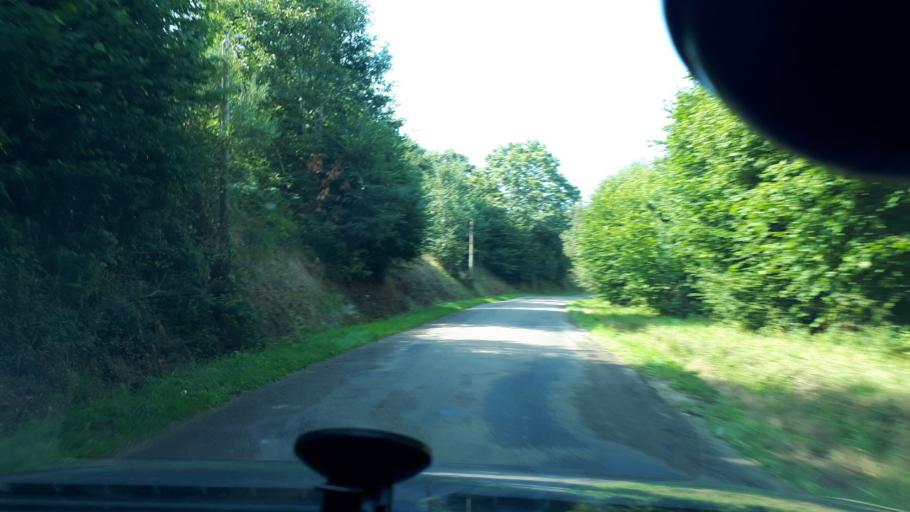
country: FR
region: Brittany
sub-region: Departement du Finistere
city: Pouldreuzic
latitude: 47.9705
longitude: -4.3676
